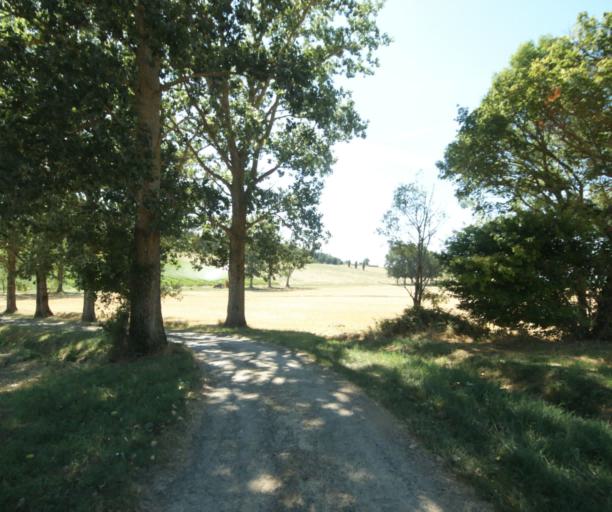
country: FR
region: Midi-Pyrenees
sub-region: Departement de la Haute-Garonne
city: Saint-Felix-Lauragais
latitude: 43.4998
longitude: 1.9300
